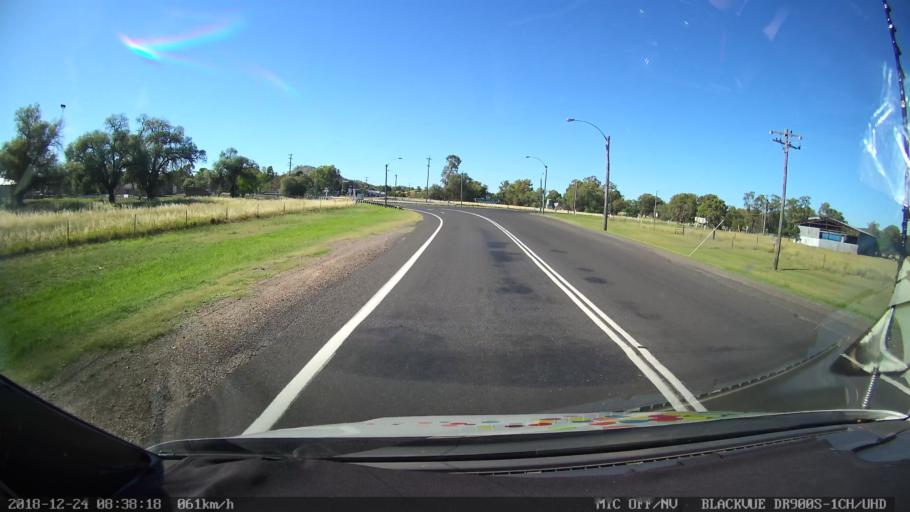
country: AU
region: New South Wales
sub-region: Liverpool Plains
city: Quirindi
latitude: -31.3399
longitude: 150.6475
